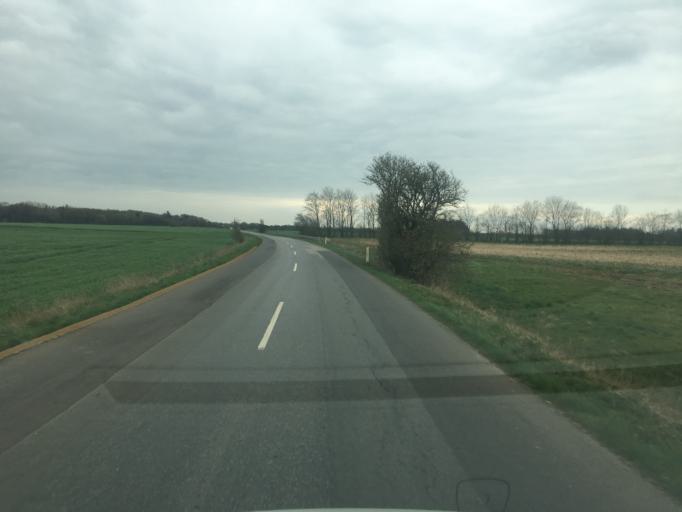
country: DK
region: South Denmark
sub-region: Aabenraa Kommune
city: Rodekro
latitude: 55.0383
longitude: 9.2057
